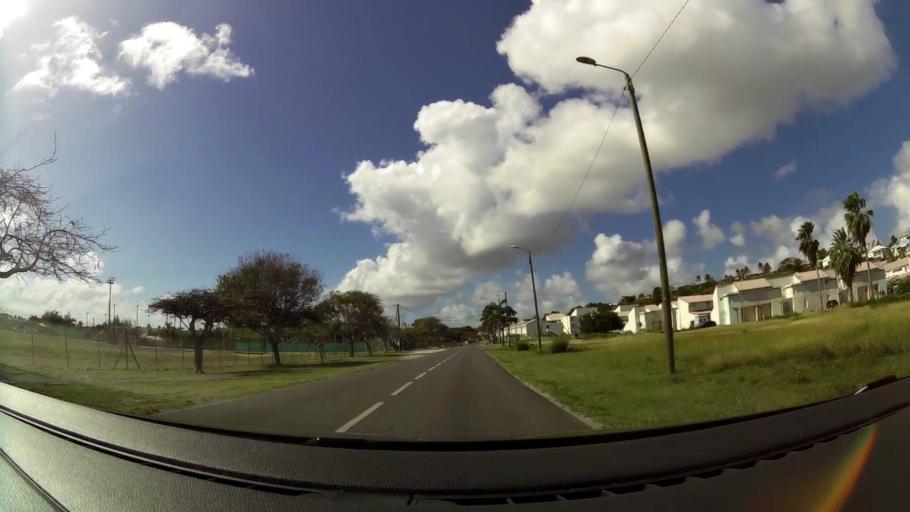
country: GP
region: Guadeloupe
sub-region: Guadeloupe
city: Saint-Francois
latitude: 16.2502
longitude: -61.2832
